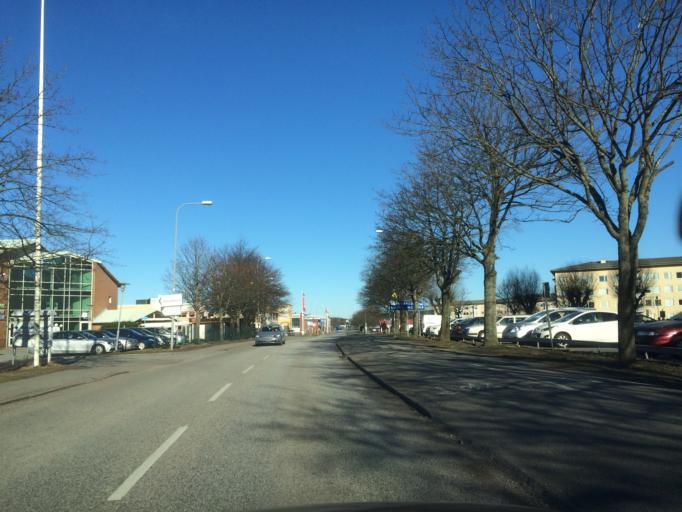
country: SE
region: Vaestra Goetaland
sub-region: Goteborg
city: Majorna
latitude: 57.6542
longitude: 11.9038
